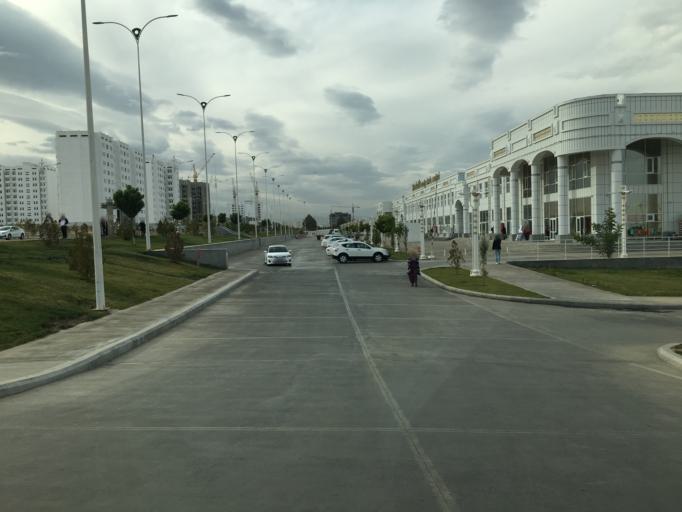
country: TM
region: Ahal
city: Ashgabat
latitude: 37.9007
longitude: 58.4151
